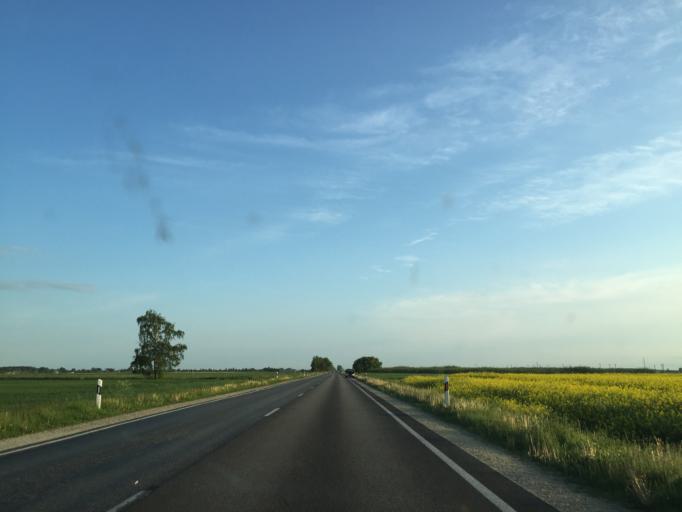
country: LT
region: Siauliu apskritis
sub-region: Joniskis
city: Joniskis
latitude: 56.0916
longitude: 23.4709
